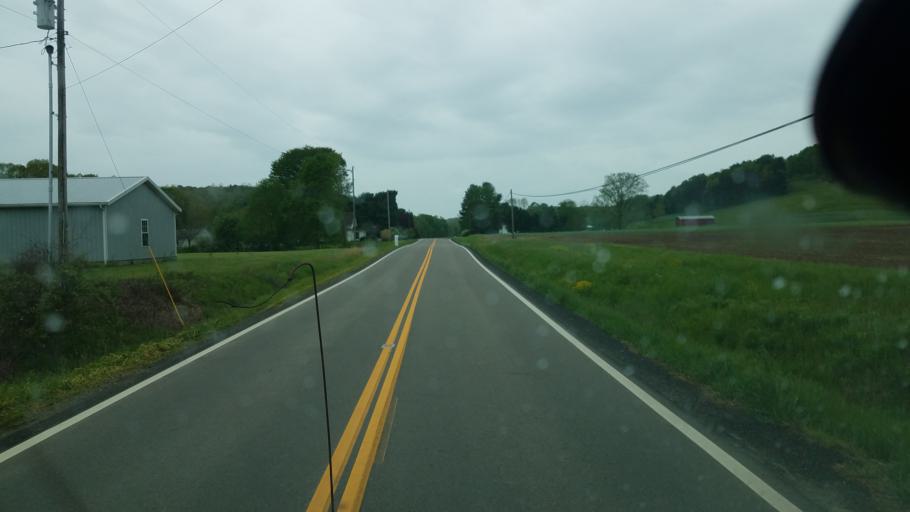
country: US
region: Ohio
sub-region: Coshocton County
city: West Lafayette
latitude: 40.2199
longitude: -81.7585
